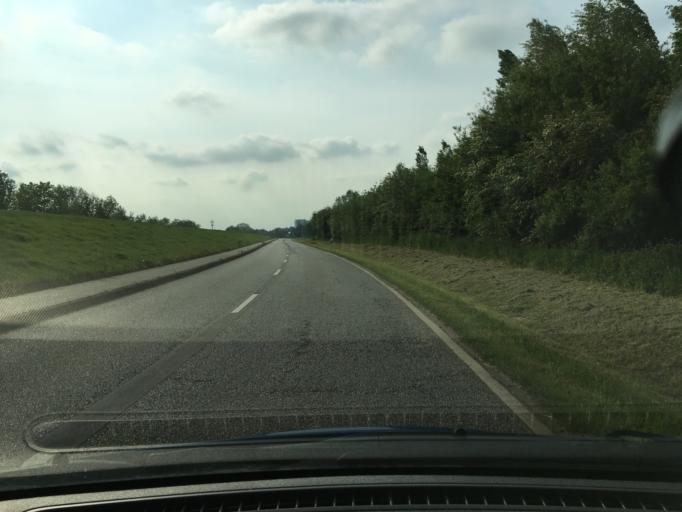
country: DE
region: Hamburg
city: Harburg
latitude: 53.4771
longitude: 10.0375
